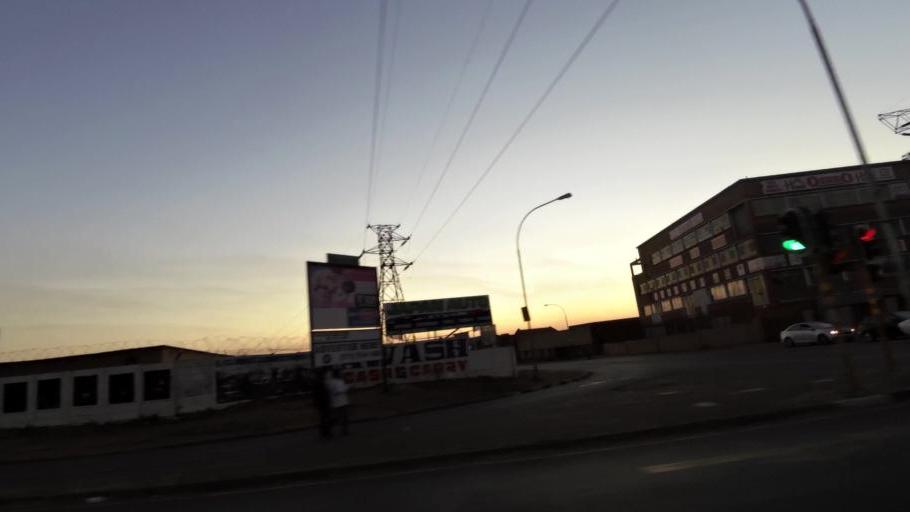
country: ZA
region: Gauteng
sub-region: City of Johannesburg Metropolitan Municipality
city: Johannesburg
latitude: -26.2124
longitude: 28.0103
